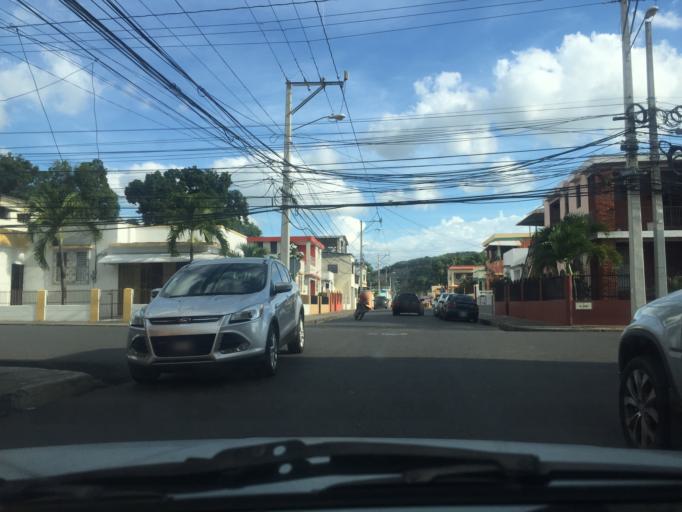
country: DO
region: Santiago
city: Santiago de los Caballeros
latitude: 19.4541
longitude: -70.7126
